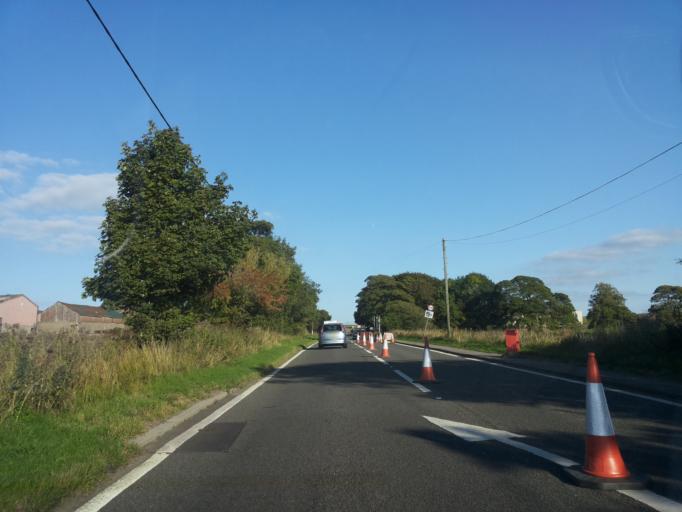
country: GB
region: England
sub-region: Derbyshire
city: Dronfield
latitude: 53.2382
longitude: -1.5466
